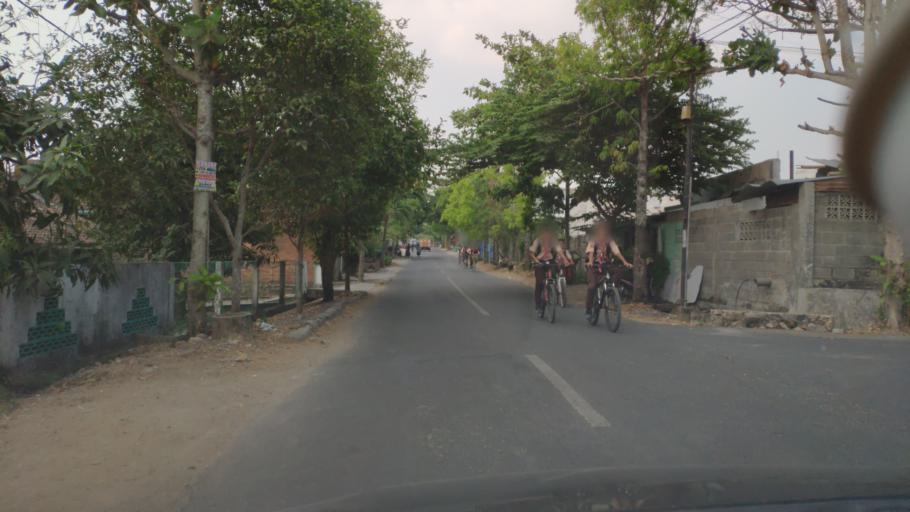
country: ID
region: Central Java
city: Kunden
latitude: -6.9604
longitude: 111.4135
